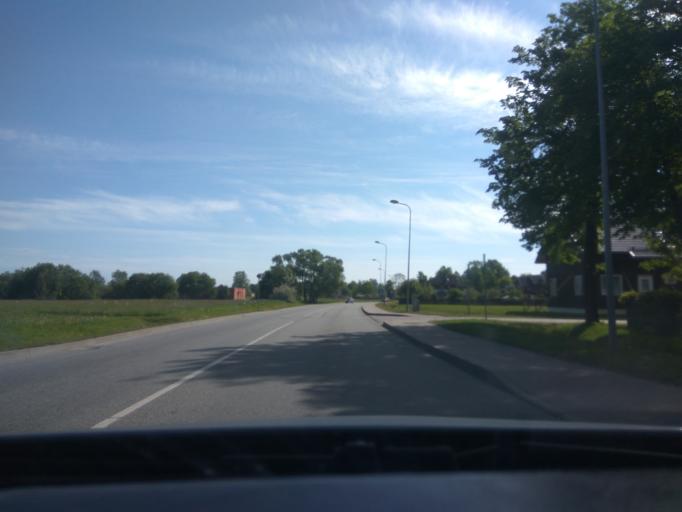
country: LV
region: Ventspils
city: Ventspils
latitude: 57.3814
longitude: 21.5745
